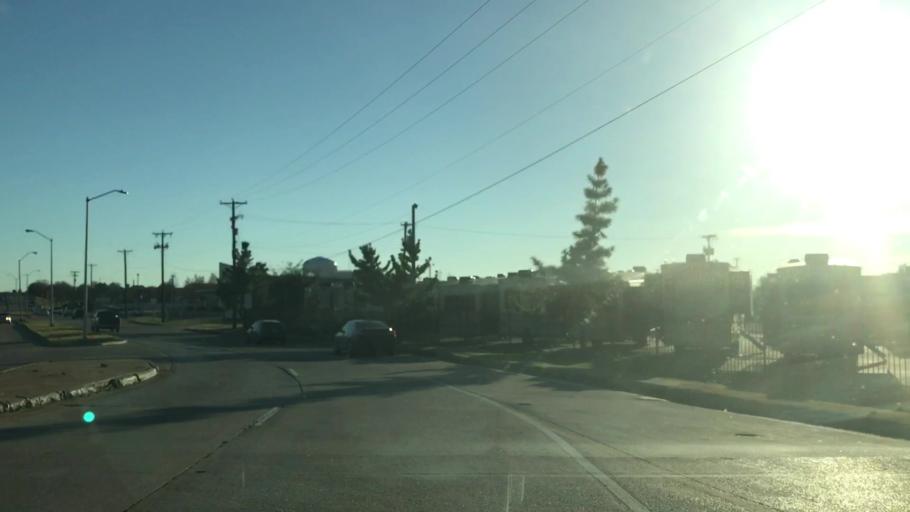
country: US
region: Texas
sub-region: Dallas County
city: Mesquite
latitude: 32.8021
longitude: -96.6682
